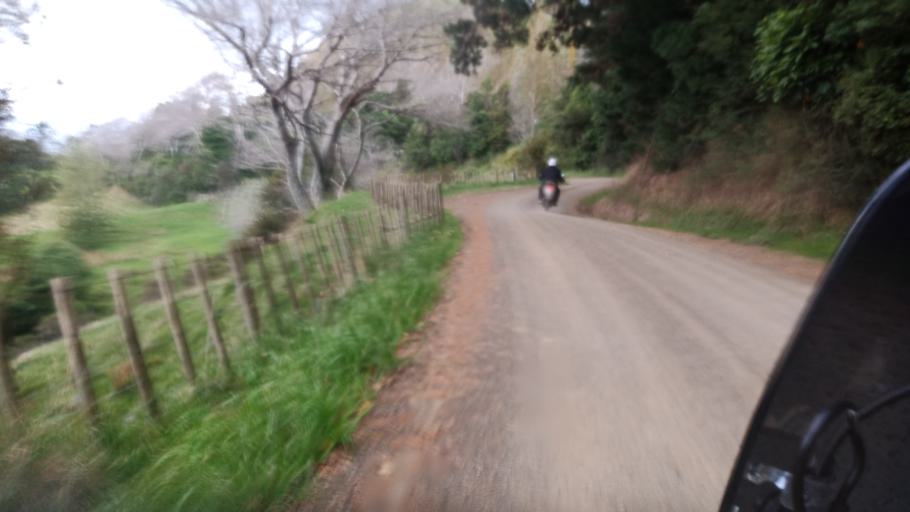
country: NZ
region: Gisborne
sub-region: Gisborne District
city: Gisborne
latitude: -38.4758
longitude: 177.6145
